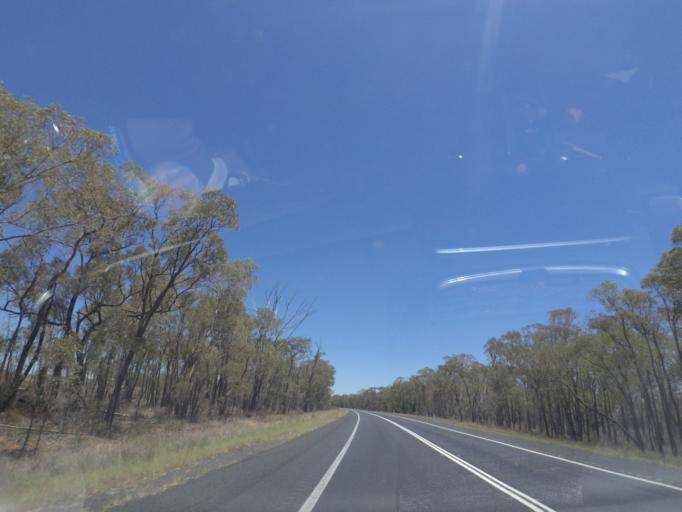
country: AU
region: New South Wales
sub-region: Warrumbungle Shire
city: Coonabarabran
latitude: -31.2067
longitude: 149.3332
